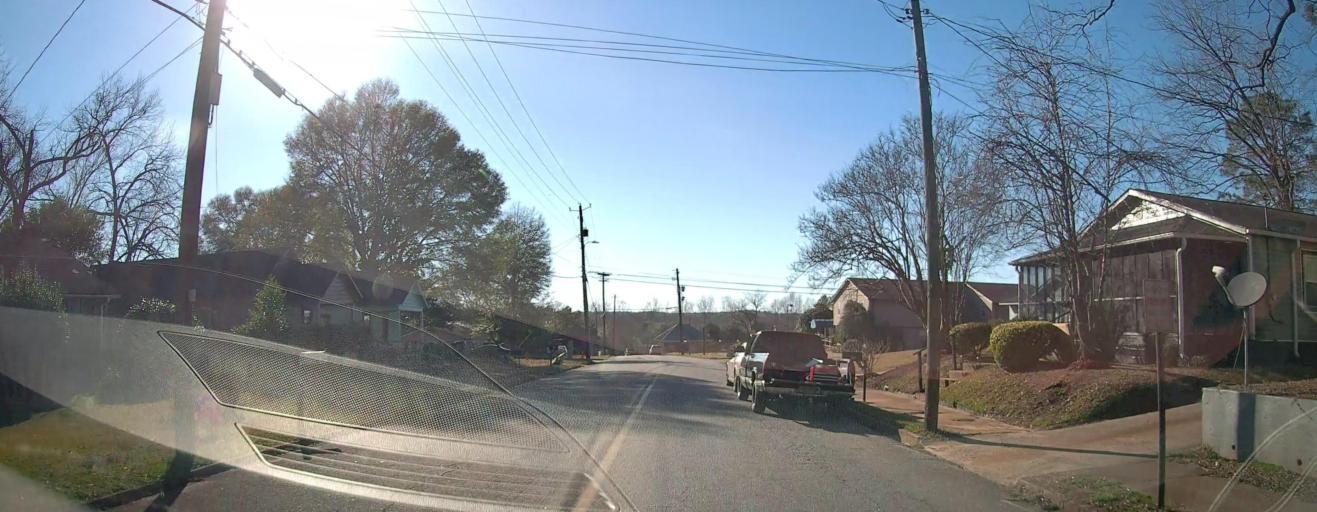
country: US
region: Georgia
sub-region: Sumter County
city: Americus
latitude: 32.0702
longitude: -84.2384
